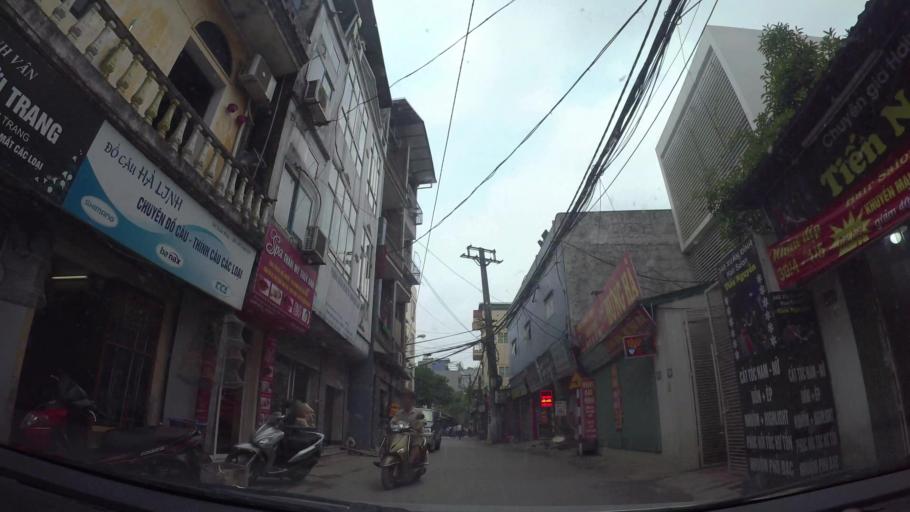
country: VN
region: Ha Noi
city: Tay Ho
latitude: 21.0711
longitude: 105.7908
